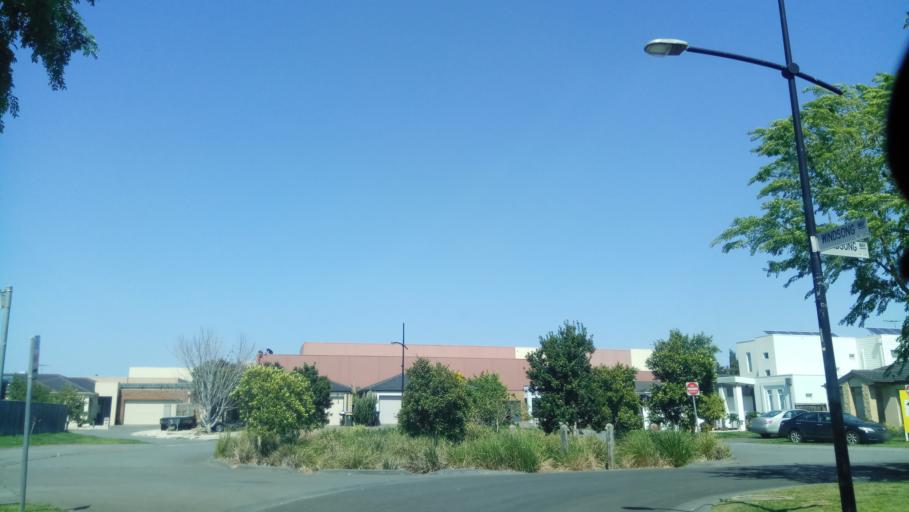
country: AU
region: Victoria
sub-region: Wyndham
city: Point Cook
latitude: -37.8941
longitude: 144.7519
